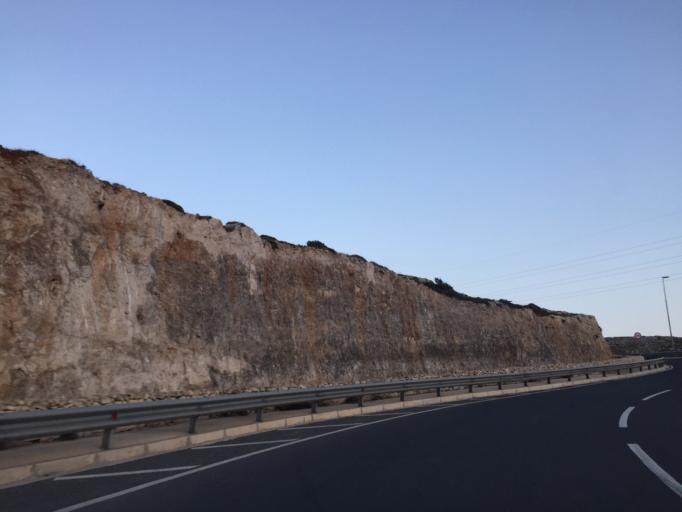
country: MT
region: Il-Mellieha
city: Mellieha
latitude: 35.9578
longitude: 14.3520
